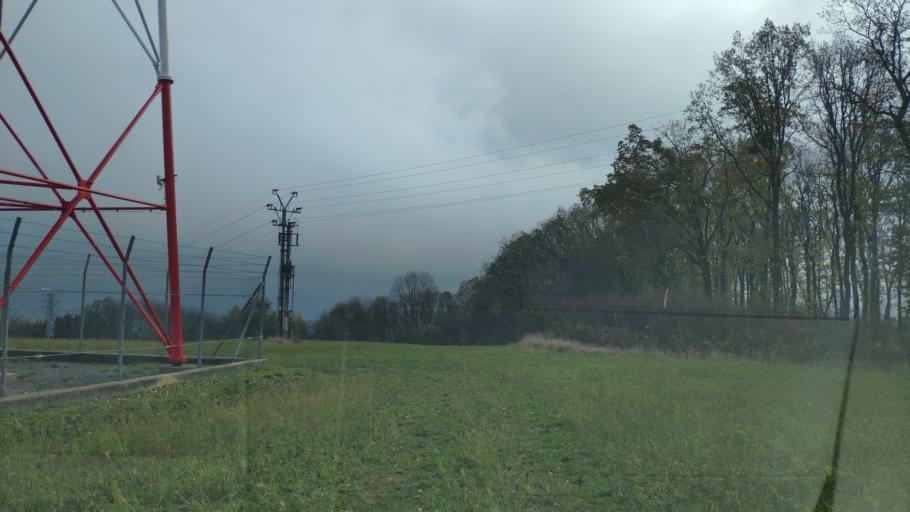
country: SK
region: Presovsky
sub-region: Okres Presov
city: Presov
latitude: 49.0042
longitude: 21.2002
